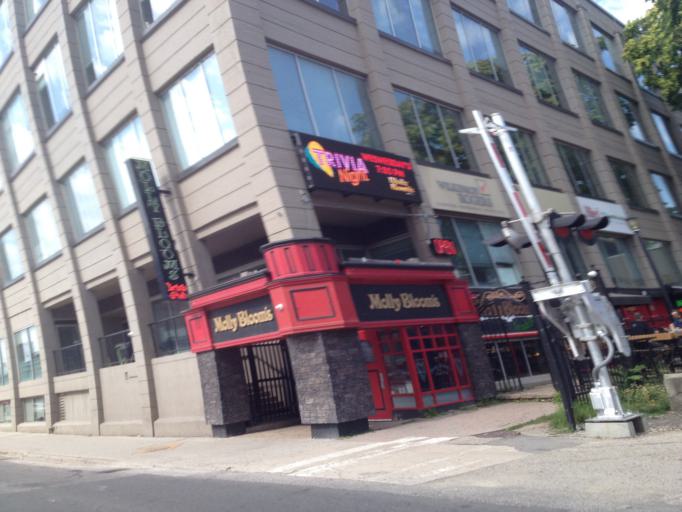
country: CA
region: Ontario
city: London
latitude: 42.9936
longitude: -81.2523
